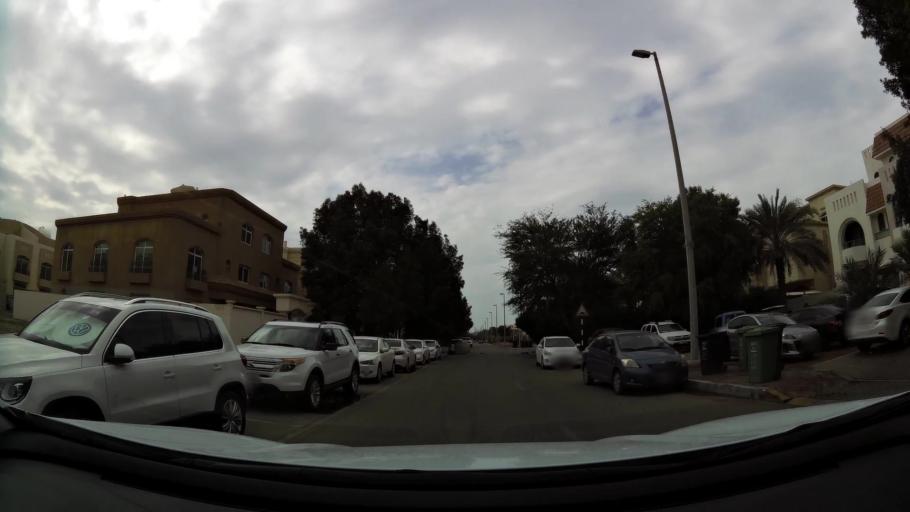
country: AE
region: Abu Dhabi
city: Abu Dhabi
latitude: 24.4315
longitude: 54.4076
